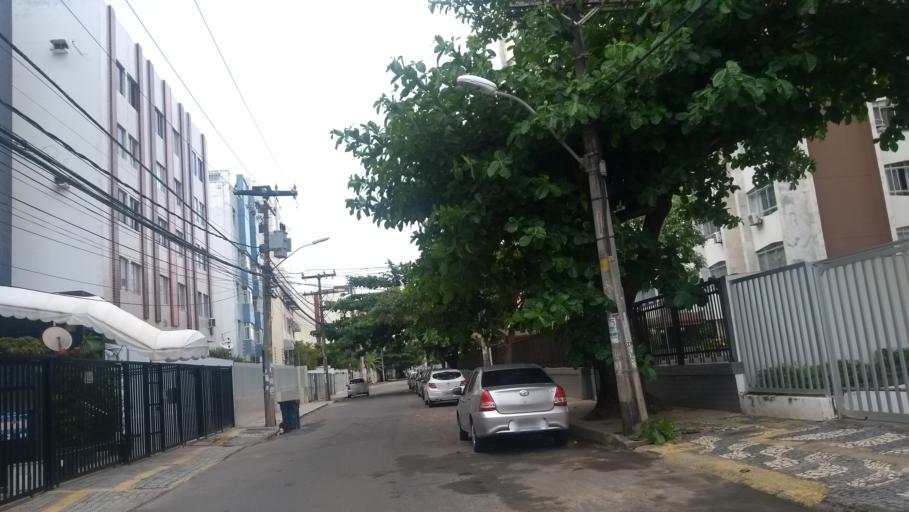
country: BR
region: Bahia
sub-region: Salvador
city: Salvador
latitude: -12.9903
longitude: -38.4472
